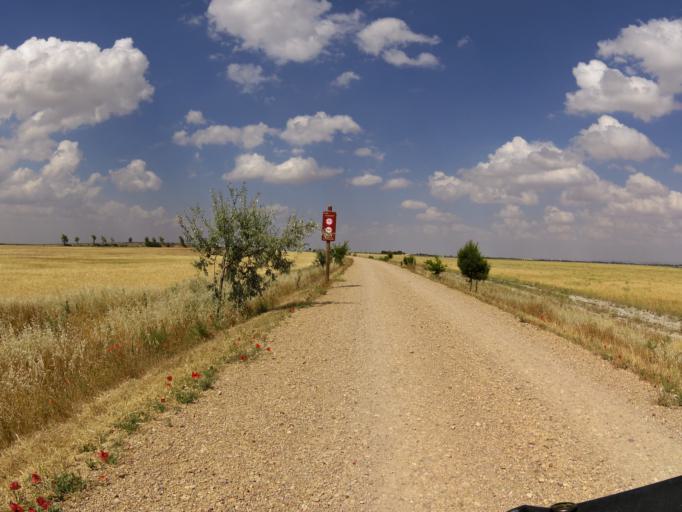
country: ES
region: Castille-La Mancha
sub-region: Provincia de Albacete
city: Albacete
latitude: 38.9409
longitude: -1.9814
